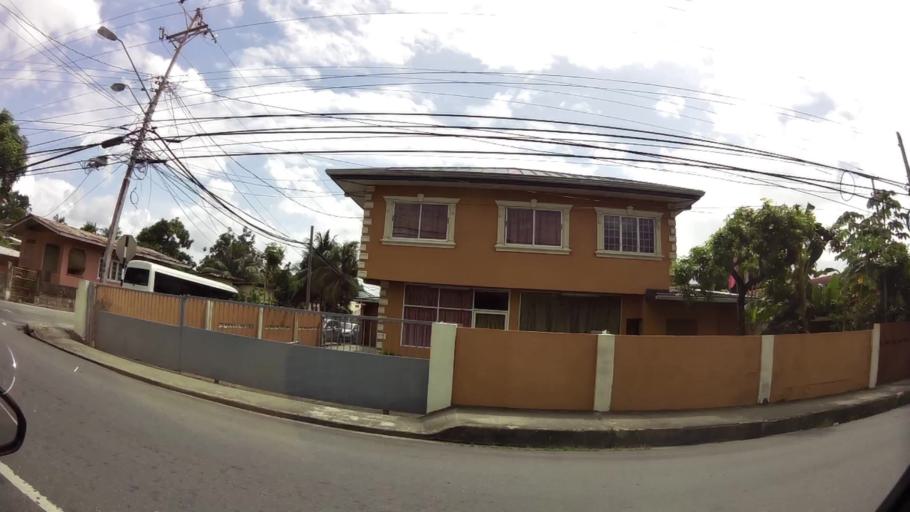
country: TT
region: Borough of Arima
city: Arima
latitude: 10.6297
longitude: -61.3021
